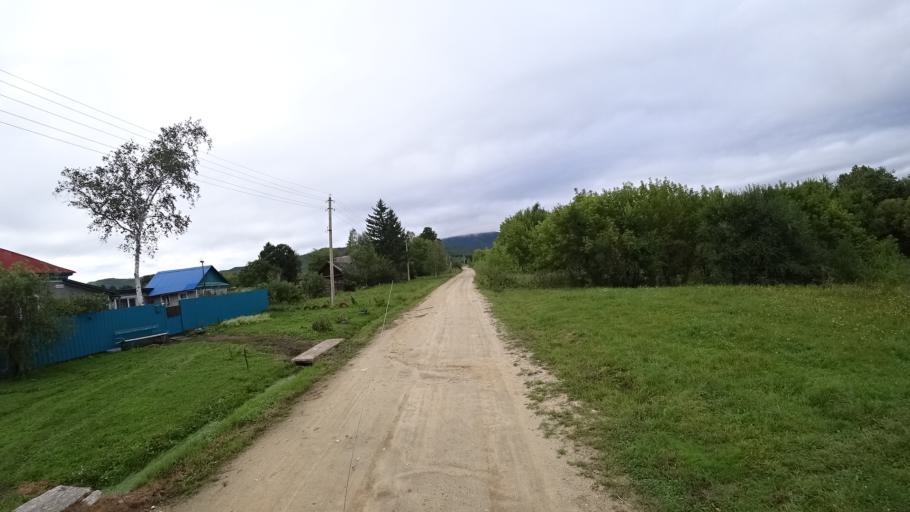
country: RU
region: Primorskiy
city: Rettikhovka
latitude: 44.1362
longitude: 132.6433
